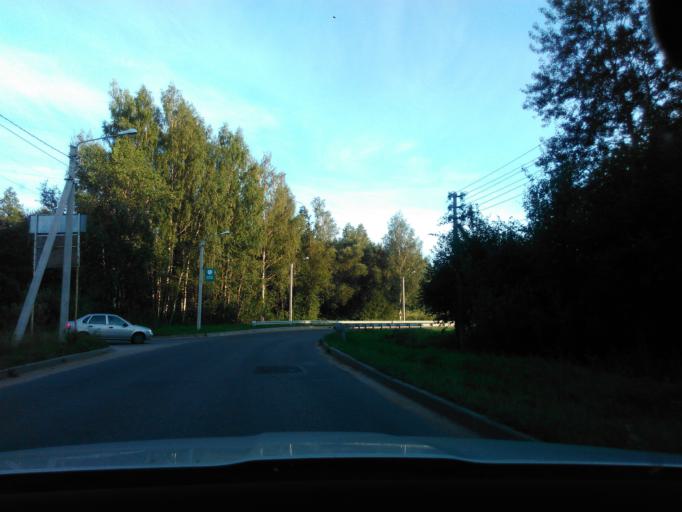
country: RU
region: Tverskaya
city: Konakovo
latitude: 56.7310
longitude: 36.7848
